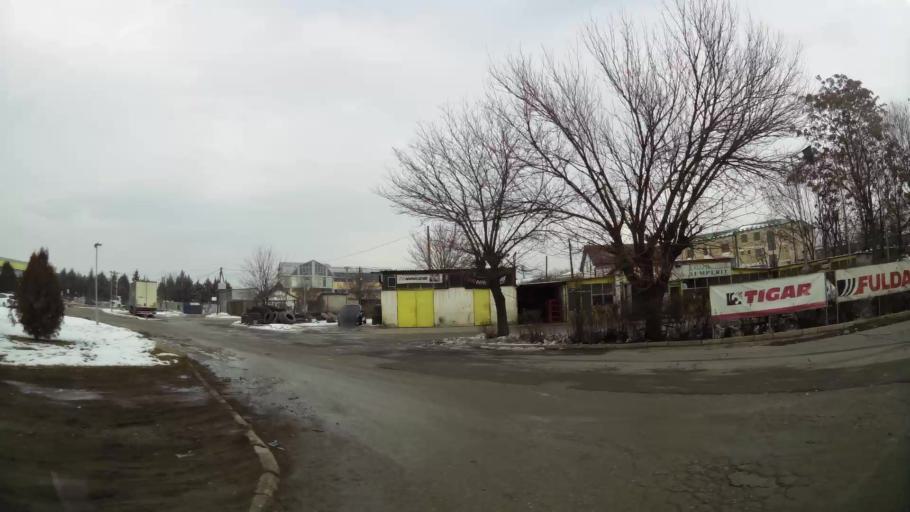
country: MK
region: Suto Orizari
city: Suto Orizare
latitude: 42.0316
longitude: 21.4045
